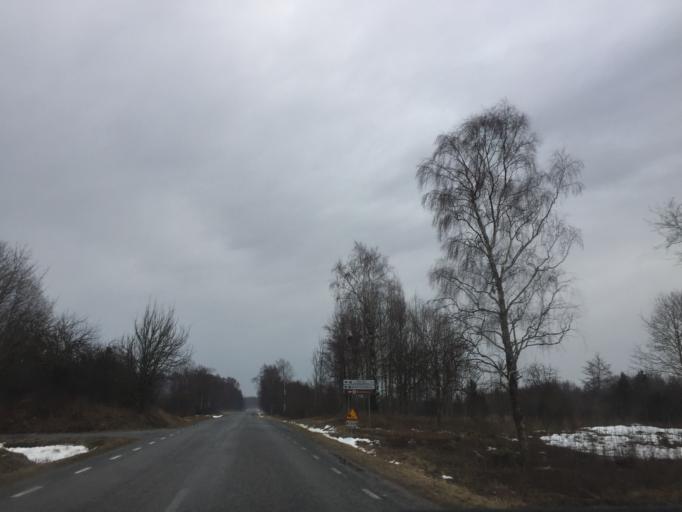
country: EE
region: Saare
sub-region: Orissaare vald
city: Orissaare
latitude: 58.5725
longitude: 23.0315
